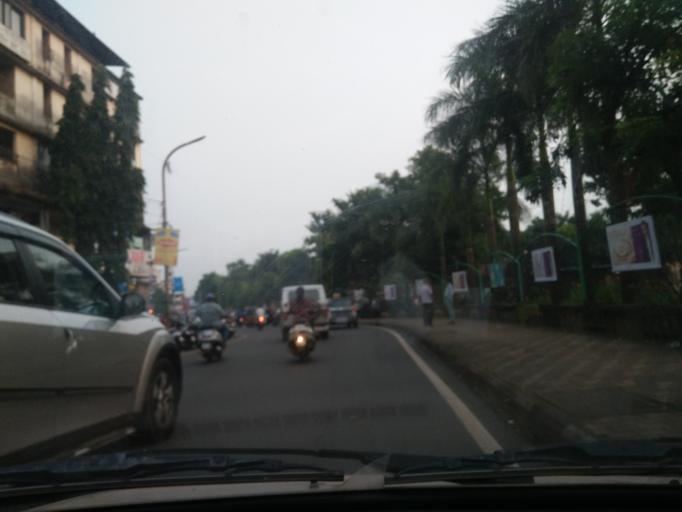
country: IN
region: Goa
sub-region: South Goa
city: Madgaon
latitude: 15.2740
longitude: 73.9582
